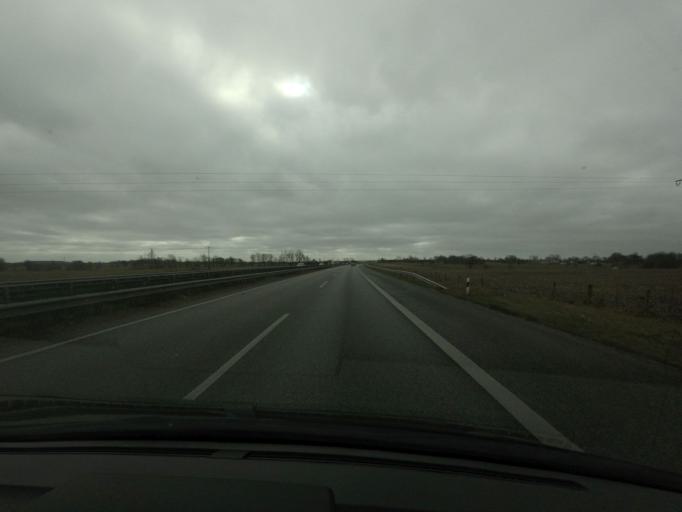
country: DE
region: Schleswig-Holstein
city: Jarplund-Weding
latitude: 54.7245
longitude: 9.3964
